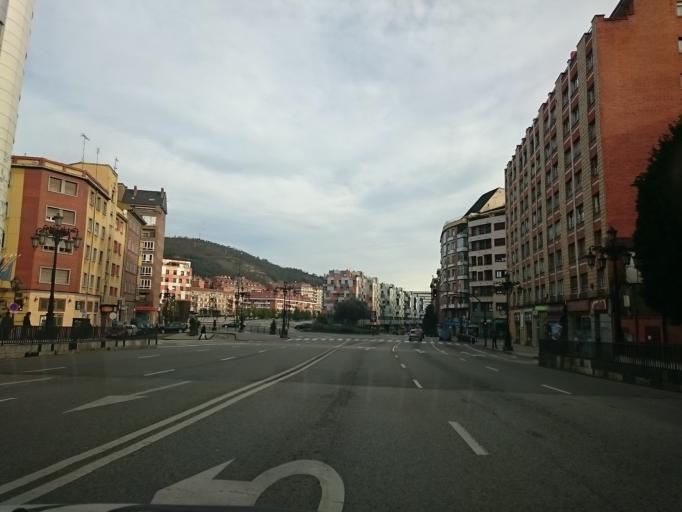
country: ES
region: Asturias
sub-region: Province of Asturias
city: Oviedo
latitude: 43.3637
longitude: -5.8605
